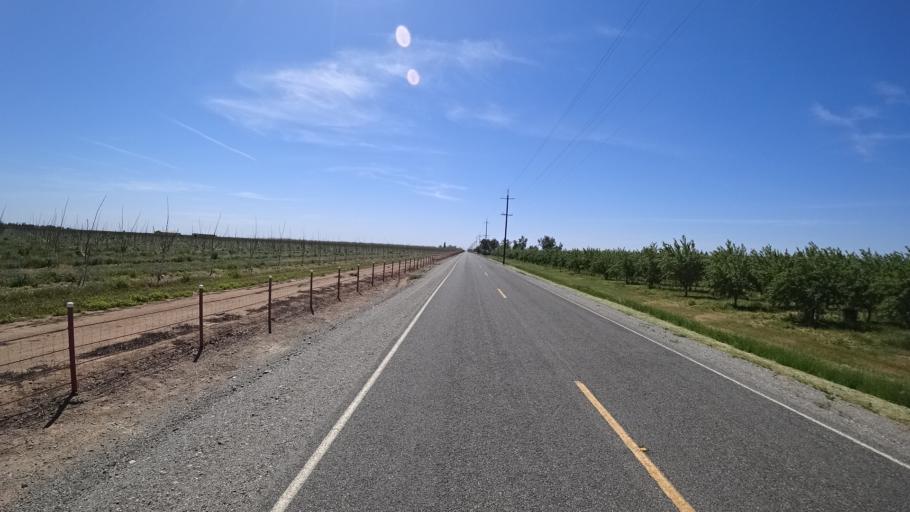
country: US
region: California
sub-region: Glenn County
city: Orland
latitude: 39.6940
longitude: -122.1779
